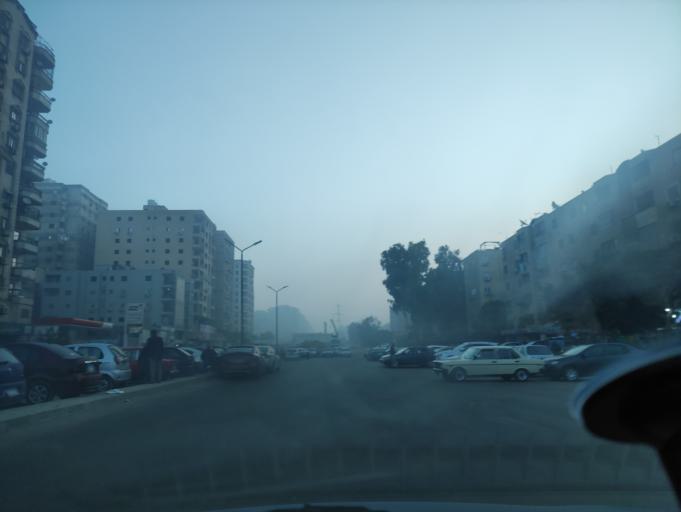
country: EG
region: Muhafazat al Qahirah
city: Cairo
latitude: 30.0470
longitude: 31.3612
